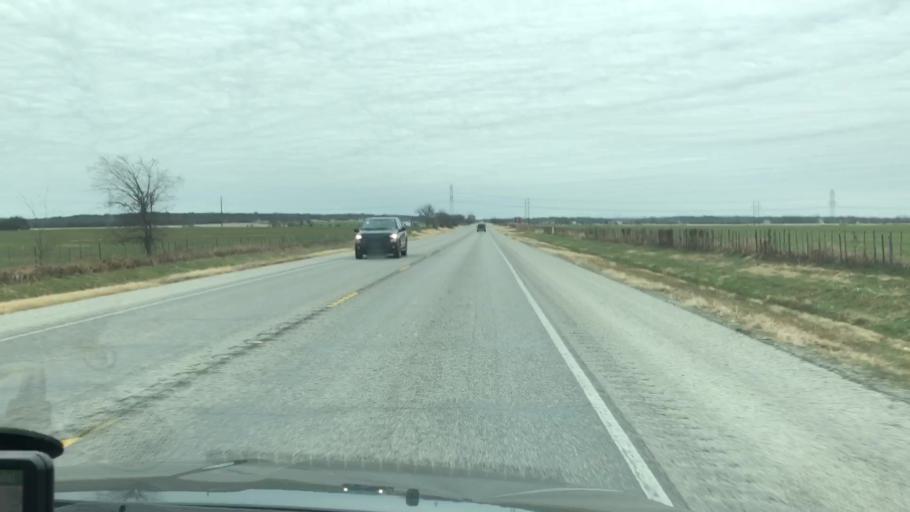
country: US
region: Texas
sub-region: Palo Pinto County
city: Mineral Wells
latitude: 32.9248
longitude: -98.0732
